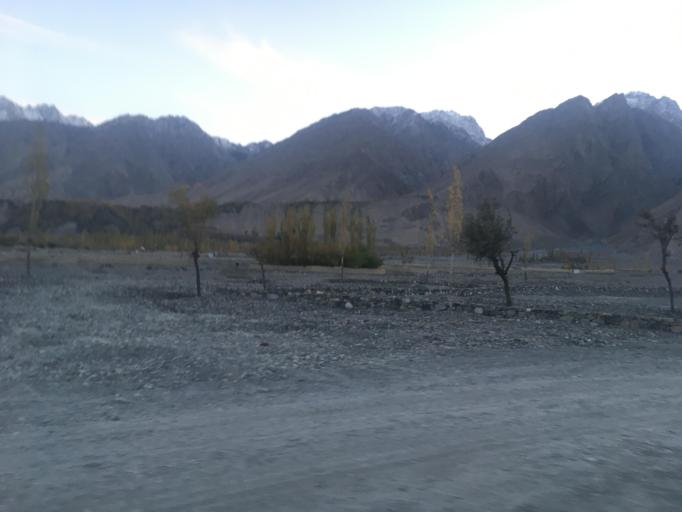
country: PK
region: Gilgit-Baltistan
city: Skardu
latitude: 35.3019
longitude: 75.5395
